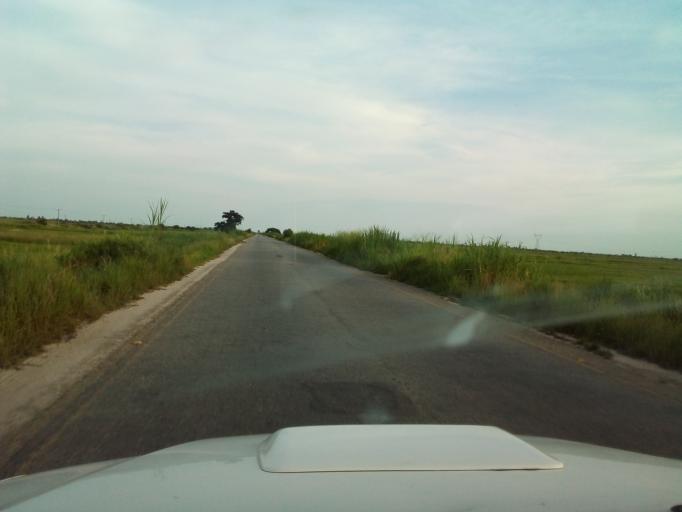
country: MZ
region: Zambezia
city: Quelimane
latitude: -17.6512
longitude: 36.8521
